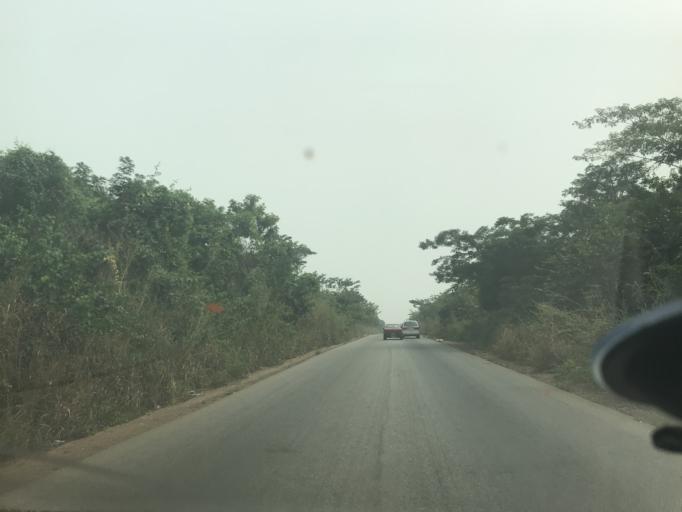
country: NG
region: Ogun
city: Ilaro
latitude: 6.8854
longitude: 3.0730
